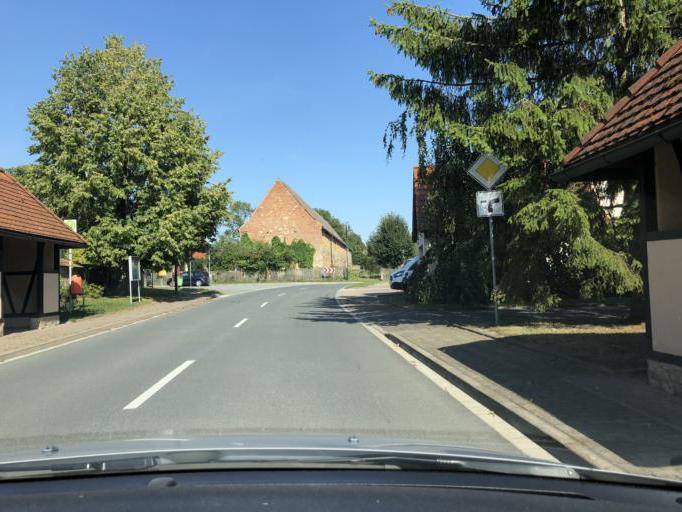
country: DE
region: Thuringia
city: Rastenberg
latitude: 51.1967
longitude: 11.4759
